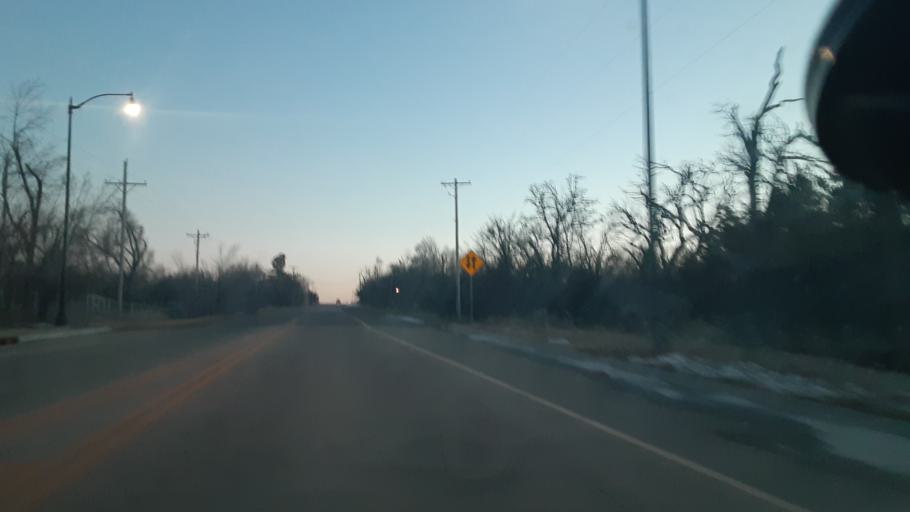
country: US
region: Oklahoma
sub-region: Oklahoma County
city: Edmond
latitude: 35.6786
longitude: -97.4250
